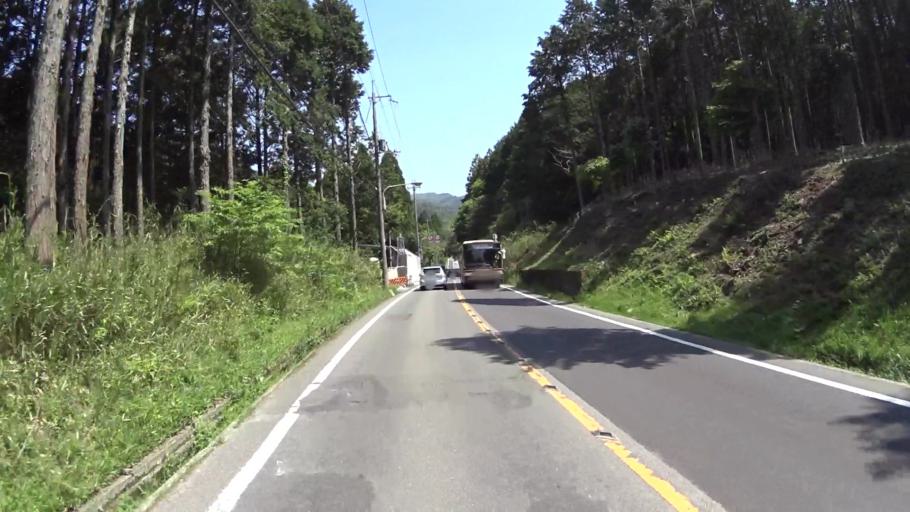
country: JP
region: Shiga Prefecture
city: Kitahama
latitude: 35.1297
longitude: 135.8334
